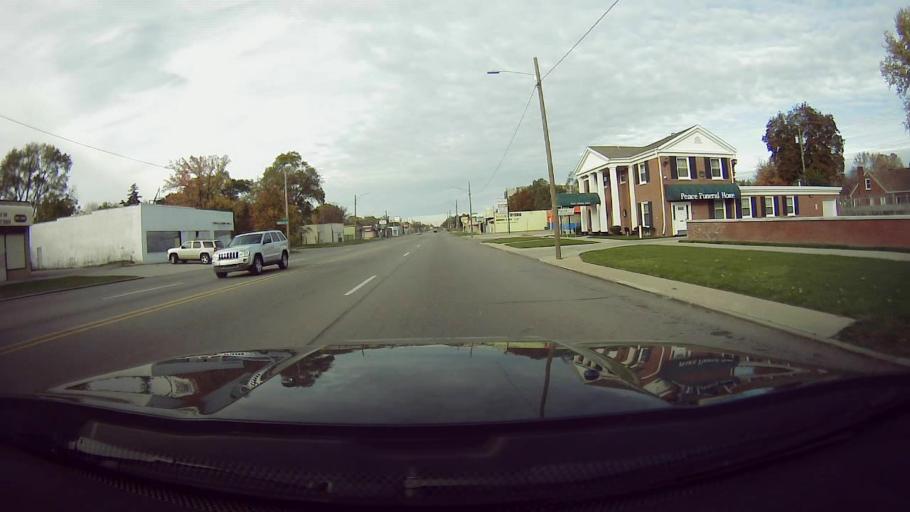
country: US
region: Michigan
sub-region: Oakland County
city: Southfield
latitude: 42.4297
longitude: -83.2349
